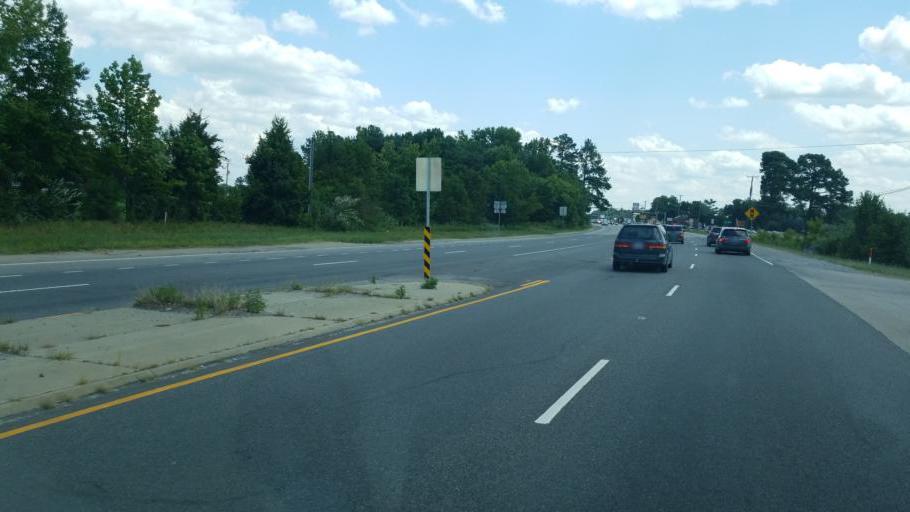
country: US
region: Virginia
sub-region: Prince George County
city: Prince George
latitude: 37.1867
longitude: -77.3228
